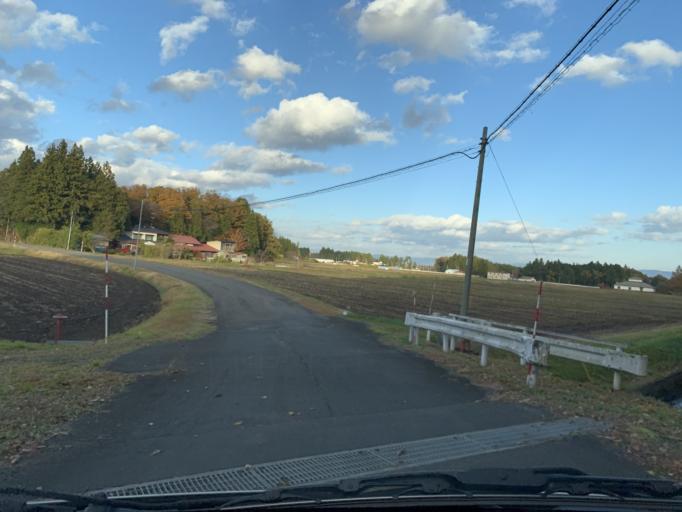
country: JP
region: Iwate
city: Mizusawa
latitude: 39.1172
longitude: 141.0261
